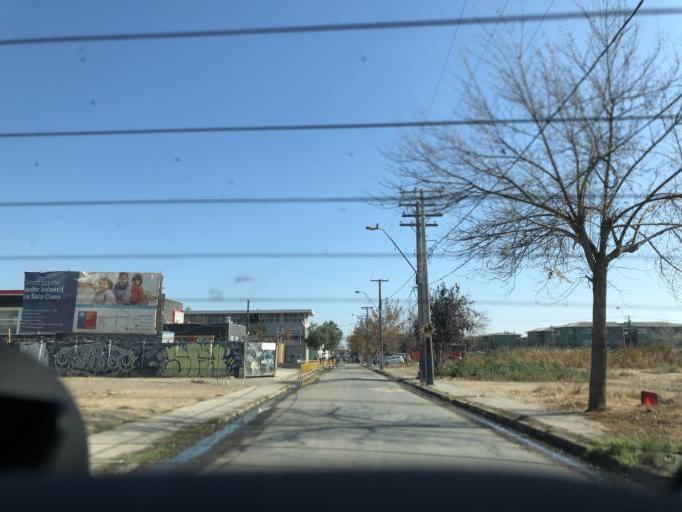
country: CL
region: Santiago Metropolitan
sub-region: Provincia de Cordillera
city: Puente Alto
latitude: -33.6268
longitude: -70.6153
